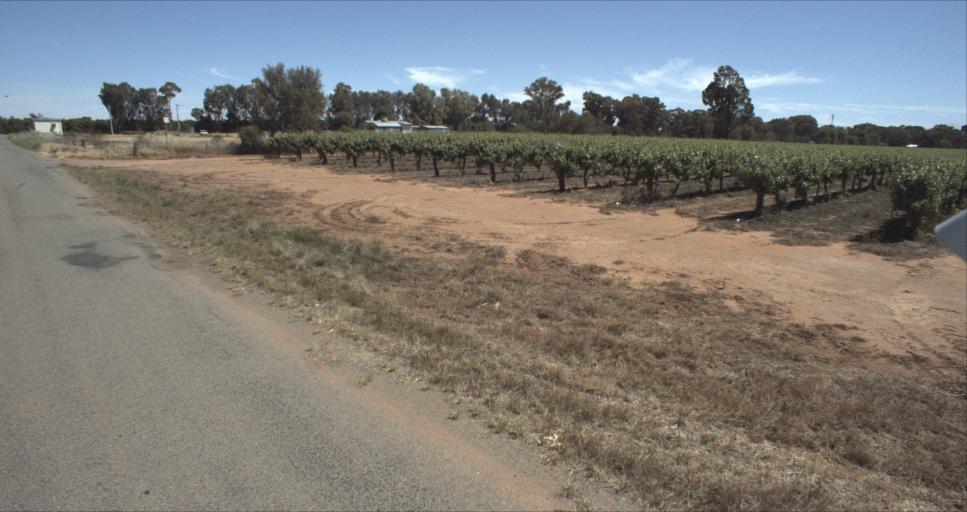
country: AU
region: New South Wales
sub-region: Leeton
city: Leeton
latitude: -34.5310
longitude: 146.3457
